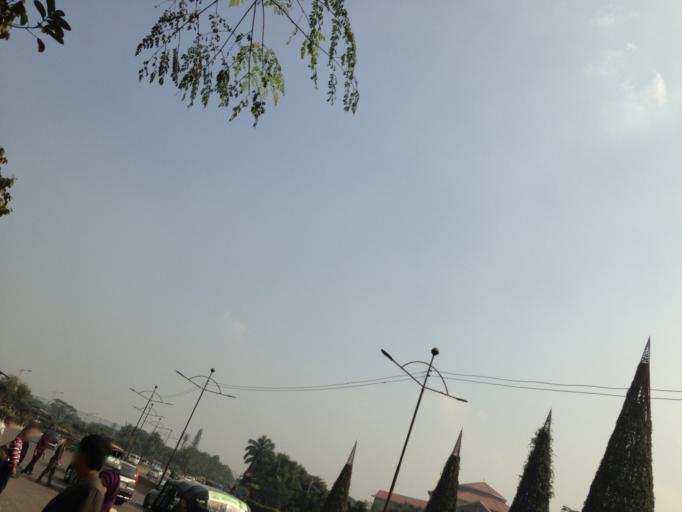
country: BD
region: Dhaka
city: Tungi
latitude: 23.8168
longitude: 90.4058
